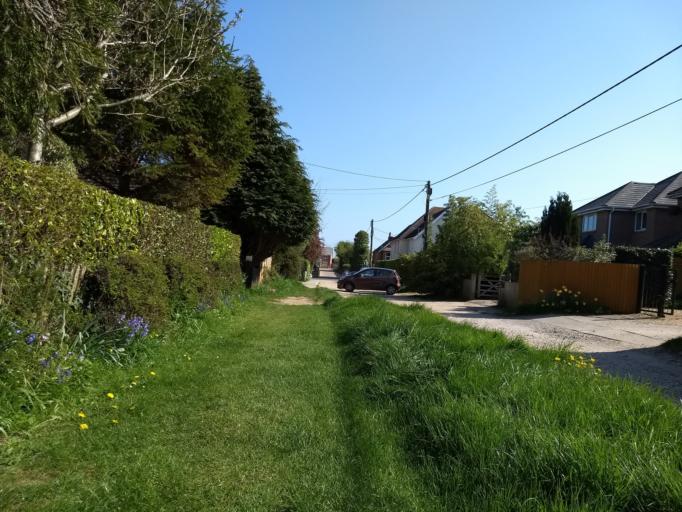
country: GB
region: England
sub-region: Isle of Wight
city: Bembridge
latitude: 50.6862
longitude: -1.0855
